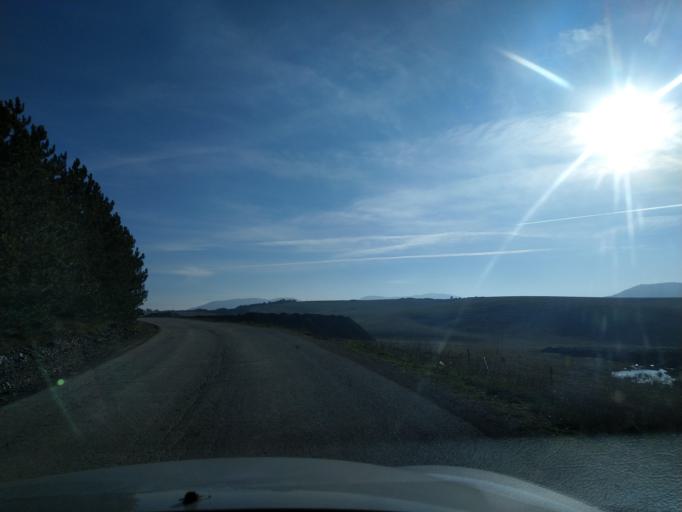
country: RS
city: Zlatibor
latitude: 43.7337
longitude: 19.6804
